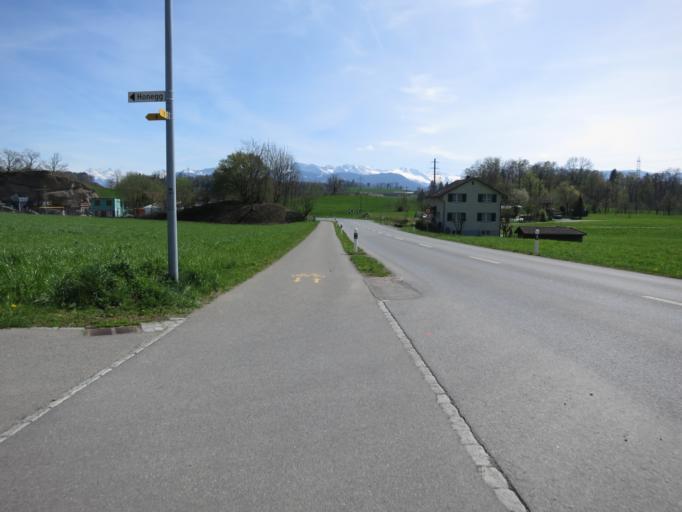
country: CH
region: Zurich
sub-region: Bezirk Hinwil
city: Rueti / Oberdorf
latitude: 47.2504
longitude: 8.8773
